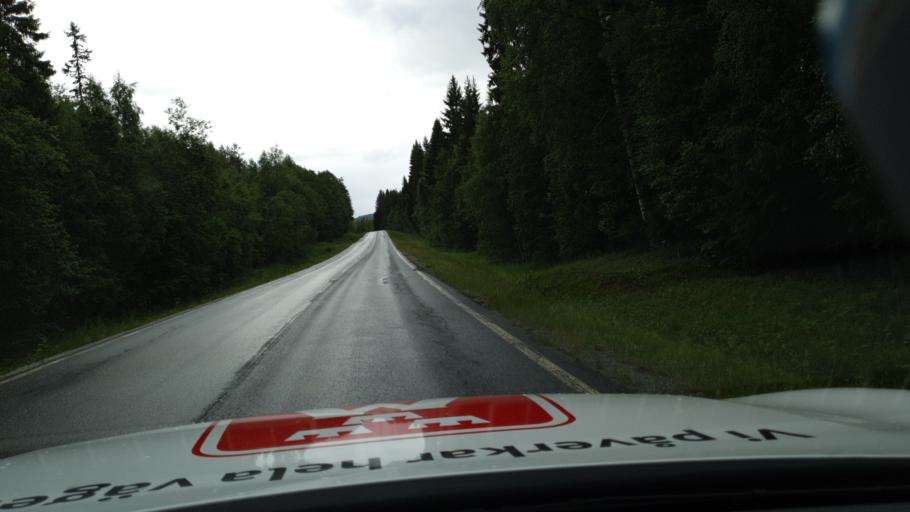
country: SE
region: Vaesterbotten
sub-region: Dorotea Kommun
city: Dorotea
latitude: 63.8644
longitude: 16.3851
